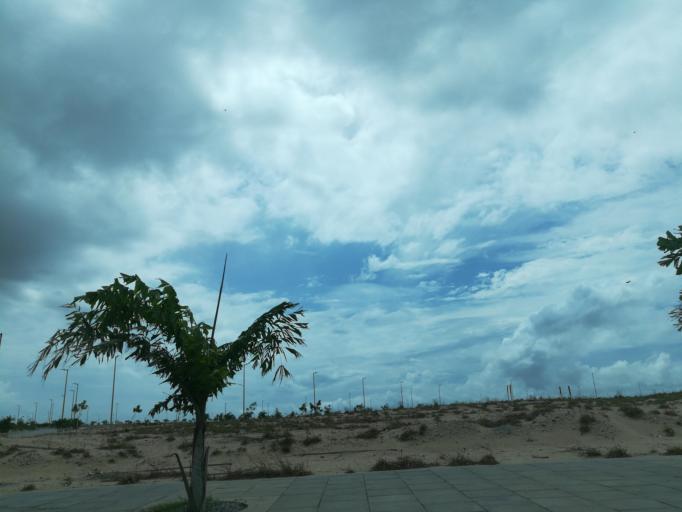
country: NG
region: Lagos
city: Lagos
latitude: 6.4109
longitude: 3.4118
